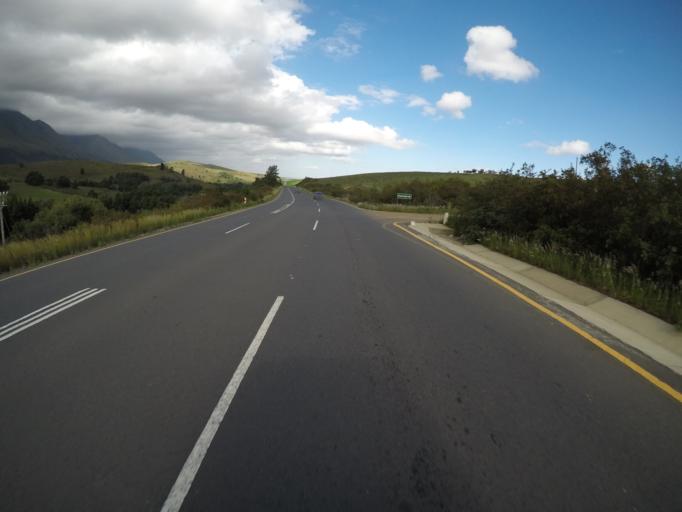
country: ZA
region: Western Cape
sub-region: Overberg District Municipality
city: Swellendam
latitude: -33.9979
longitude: 20.3575
